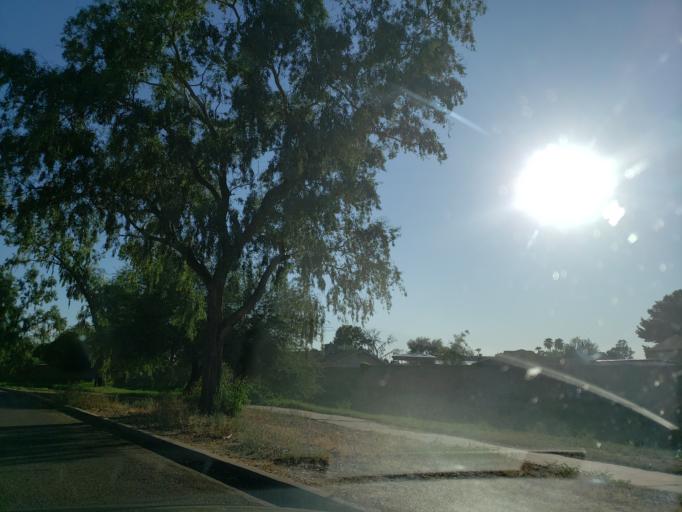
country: US
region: Arizona
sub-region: Maricopa County
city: Paradise Valley
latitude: 33.6032
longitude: -111.9912
